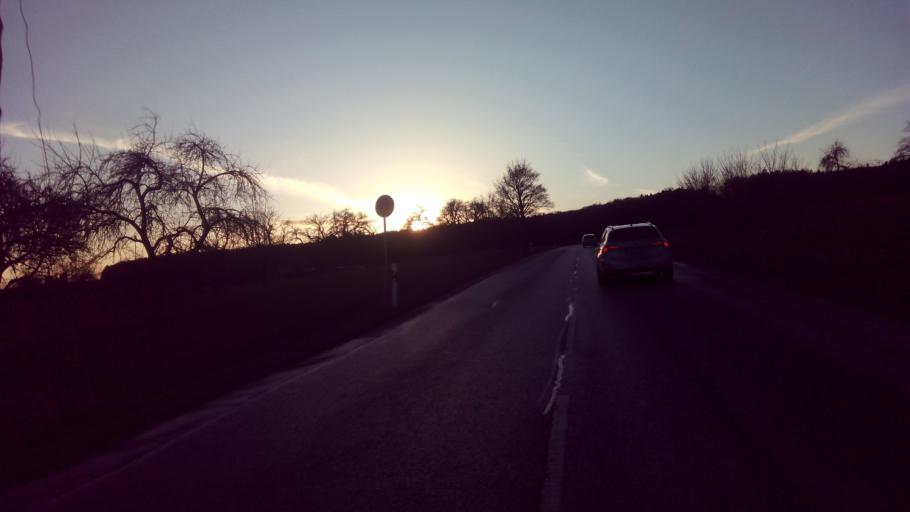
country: DE
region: Baden-Wuerttemberg
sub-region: Tuebingen Region
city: Altheim
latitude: 48.3455
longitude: 9.8076
